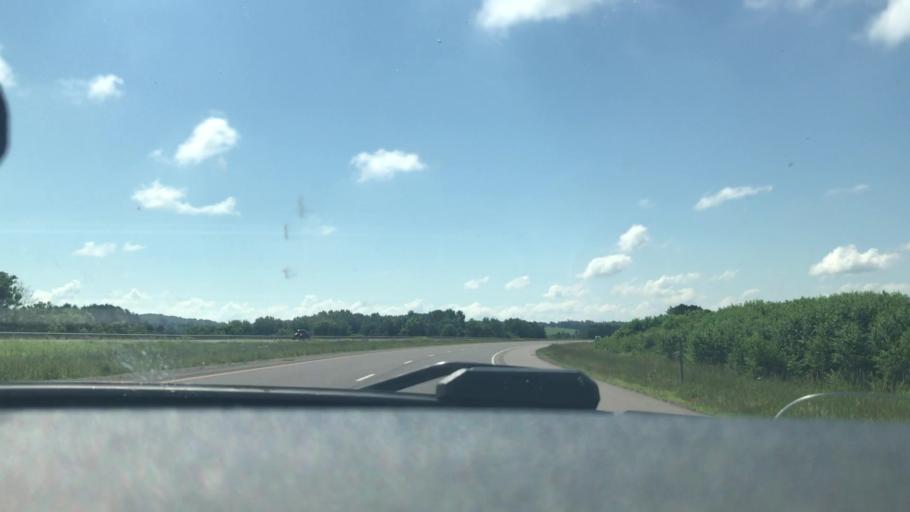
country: US
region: Wisconsin
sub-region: Chippewa County
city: Bloomer
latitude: 45.0665
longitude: -91.4672
